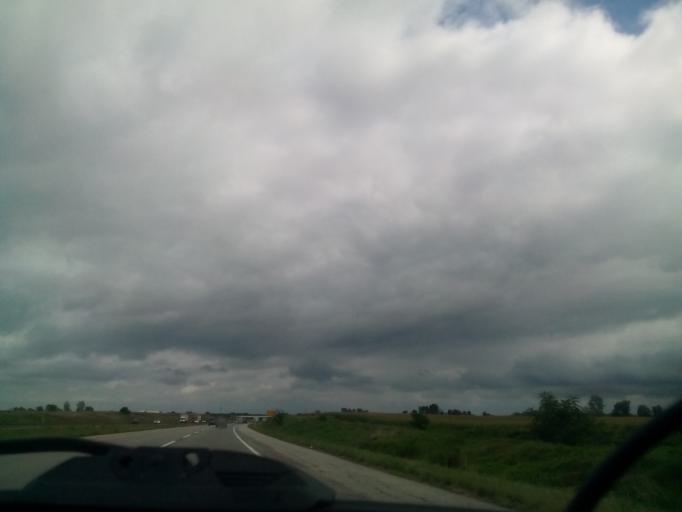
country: US
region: Indiana
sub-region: Steuben County
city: Fremont
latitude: 41.6855
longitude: -84.8853
